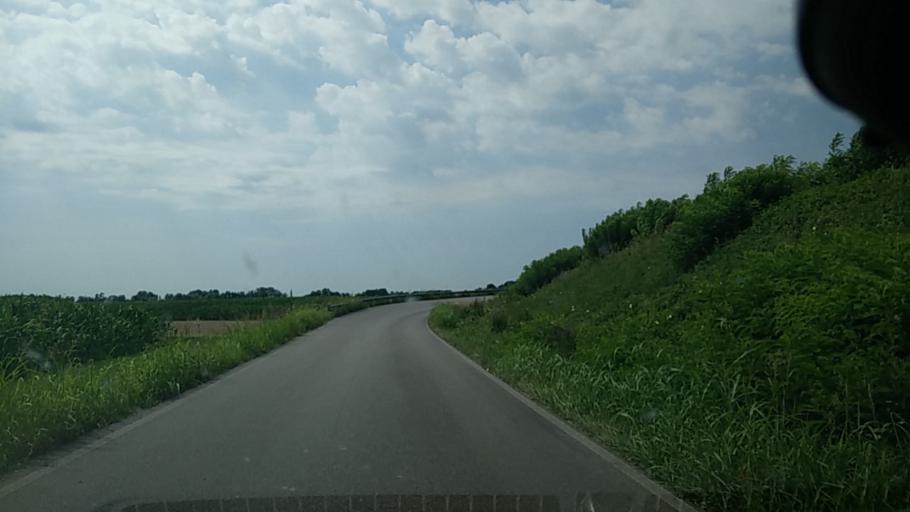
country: IT
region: Friuli Venezia Giulia
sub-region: Provincia di Pordenone
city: Puia-Villanova
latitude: 45.8318
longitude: 12.5736
